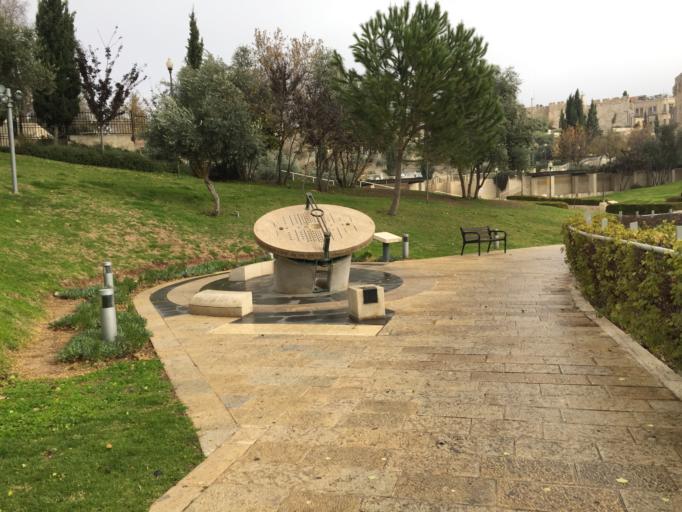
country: PS
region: West Bank
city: Old City
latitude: 31.7751
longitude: 35.2260
